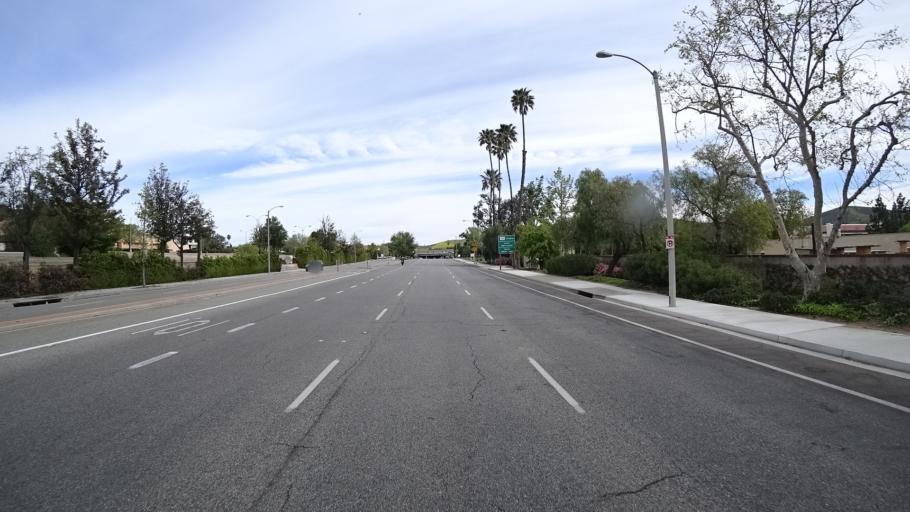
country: US
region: California
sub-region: Ventura County
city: Thousand Oaks
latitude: 34.1631
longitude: -118.8380
